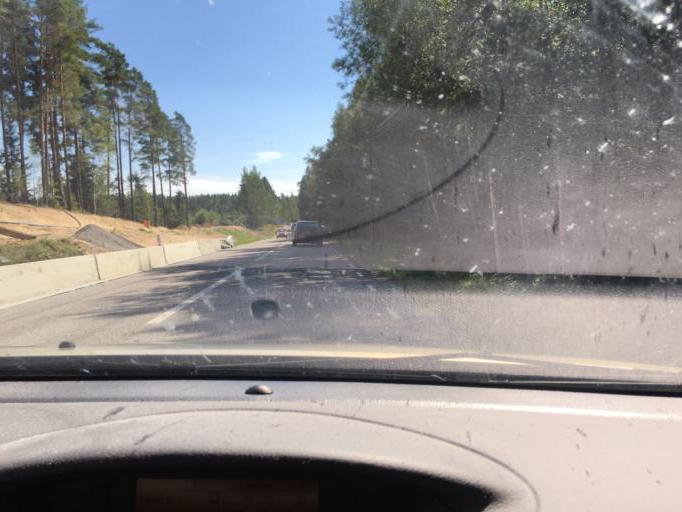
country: SE
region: Stockholm
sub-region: Varmdo Kommun
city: Mortnas
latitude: 59.2755
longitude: 18.4568
